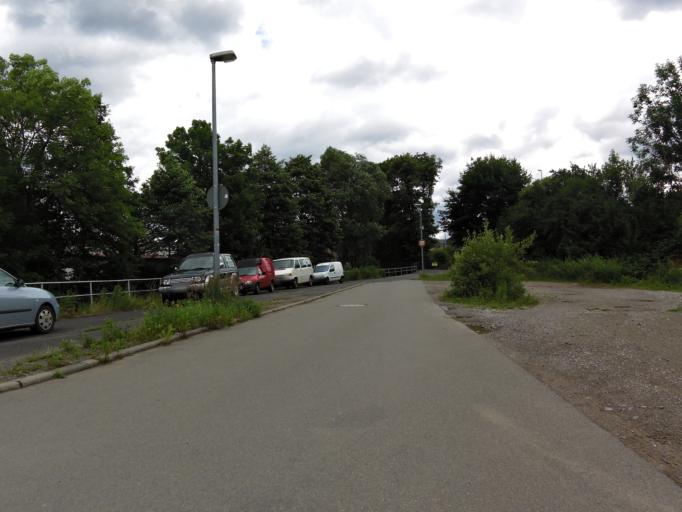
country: DE
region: Thuringia
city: Schmalkalden
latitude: 50.7200
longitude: 10.4347
